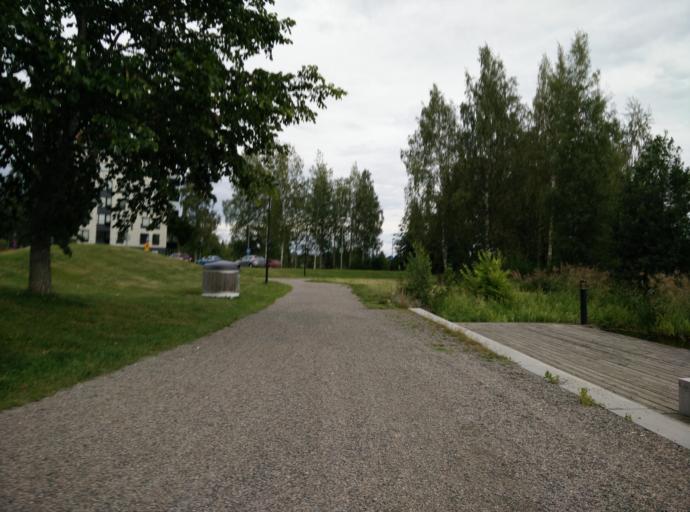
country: FI
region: Haeme
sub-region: Haemeenlinna
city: Haemeenlinna
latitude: 60.9947
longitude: 24.4789
